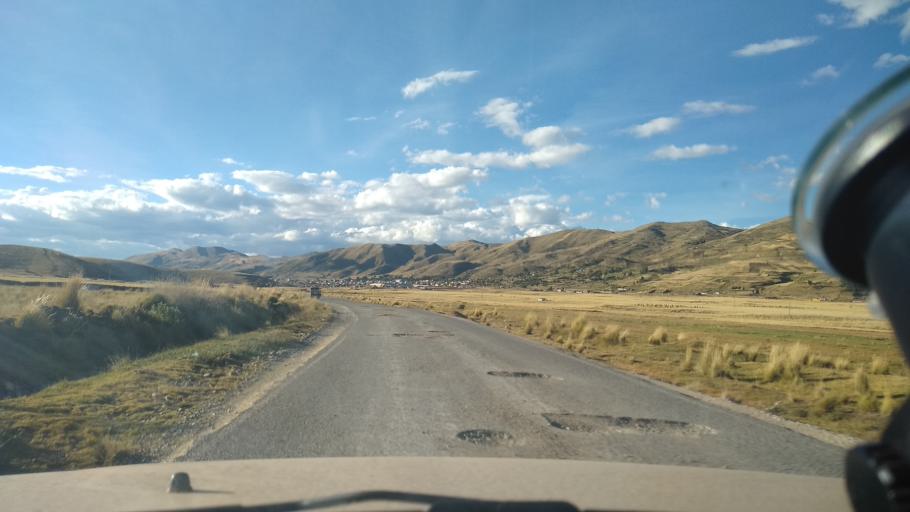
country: PE
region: Cusco
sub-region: Provincia de Canas
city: Chignayhua
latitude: -14.2408
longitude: -71.4329
